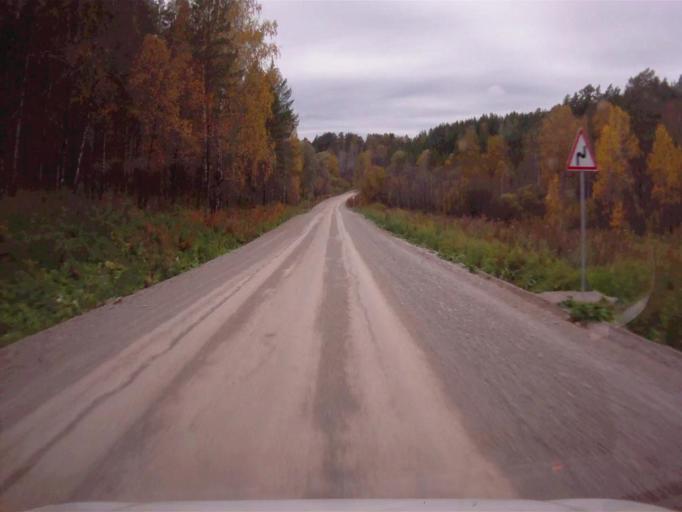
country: RU
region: Chelyabinsk
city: Nyazepetrovsk
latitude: 56.0571
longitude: 59.4633
